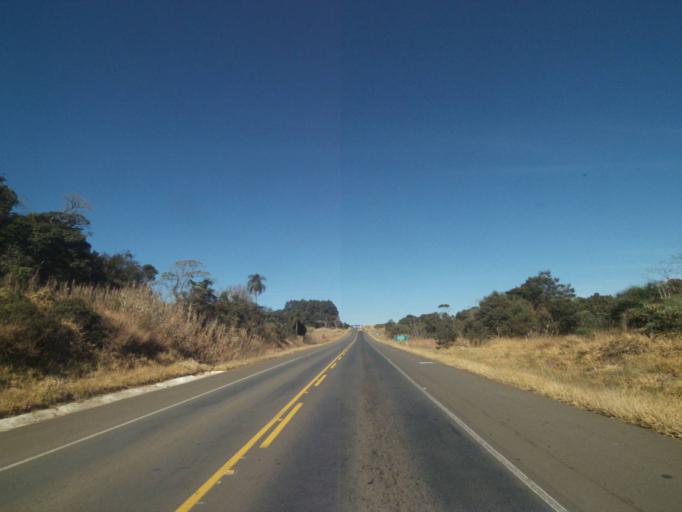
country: BR
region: Parana
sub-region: Tibagi
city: Tibagi
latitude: -24.7575
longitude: -50.4699
